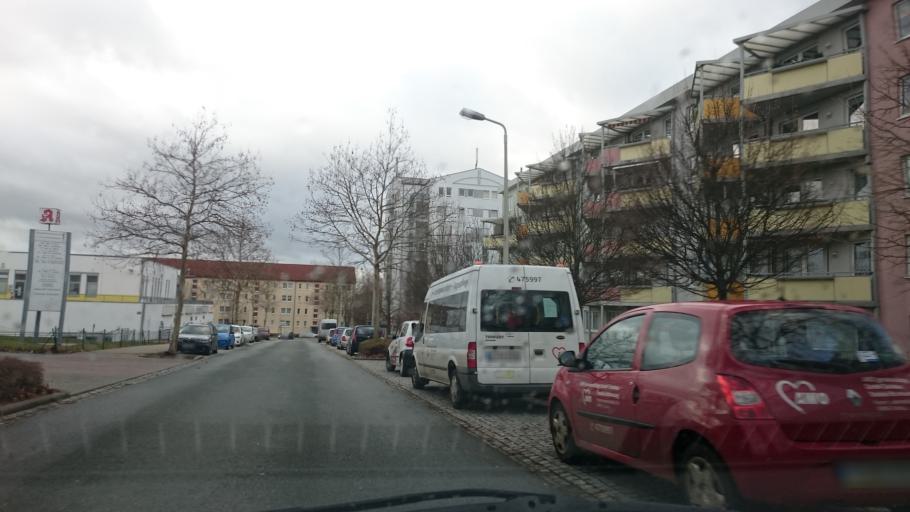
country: DE
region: Saxony
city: Zwickau
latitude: 50.7357
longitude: 12.5088
